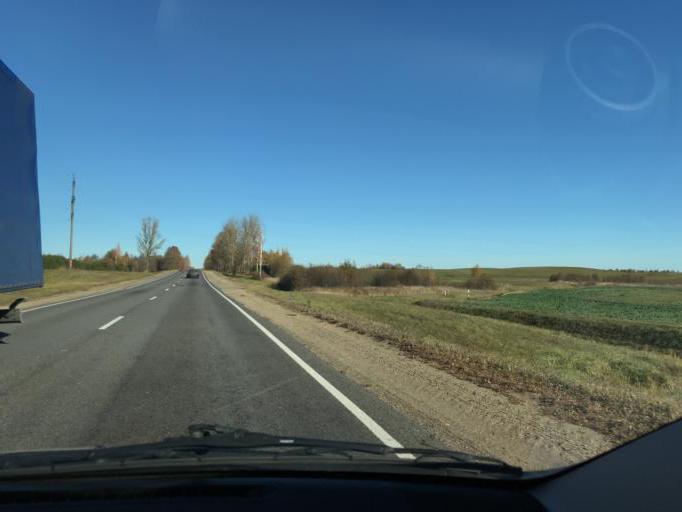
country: BY
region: Vitebsk
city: Lyepyel'
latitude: 55.0118
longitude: 28.7400
